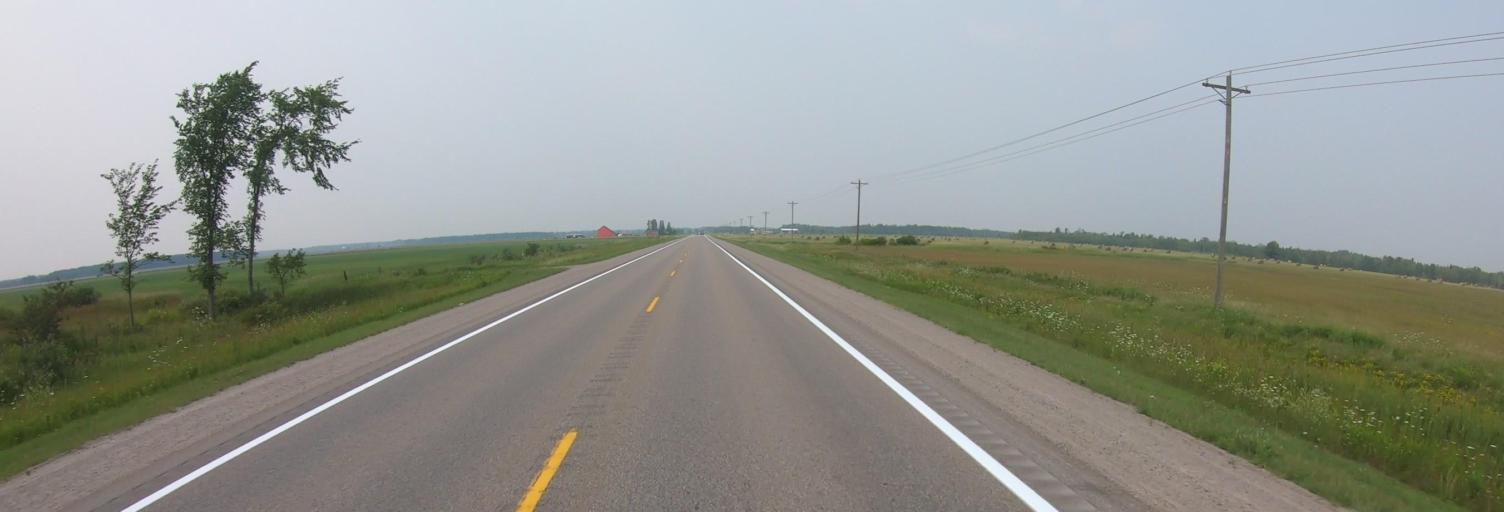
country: US
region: Michigan
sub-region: Chippewa County
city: Sault Ste. Marie
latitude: 46.3490
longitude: -84.3639
